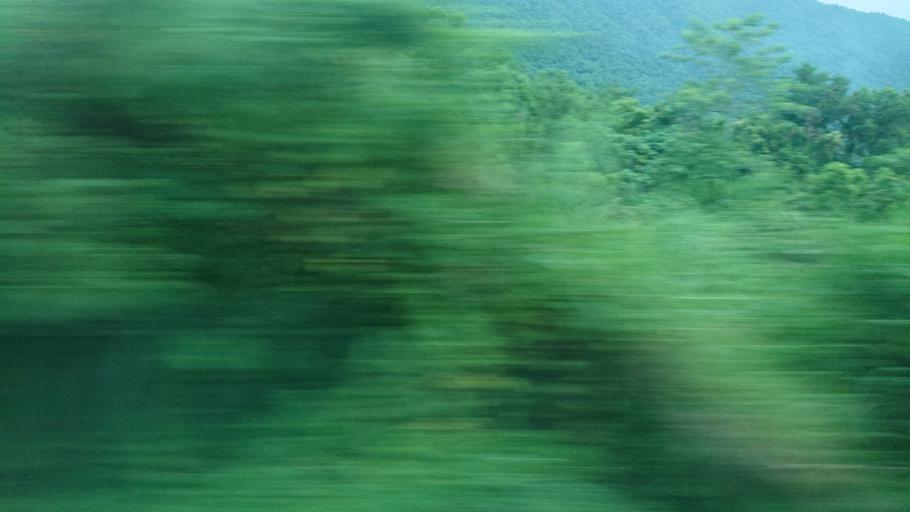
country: TW
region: Taiwan
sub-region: Hualien
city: Hualian
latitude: 24.1151
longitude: 121.6271
